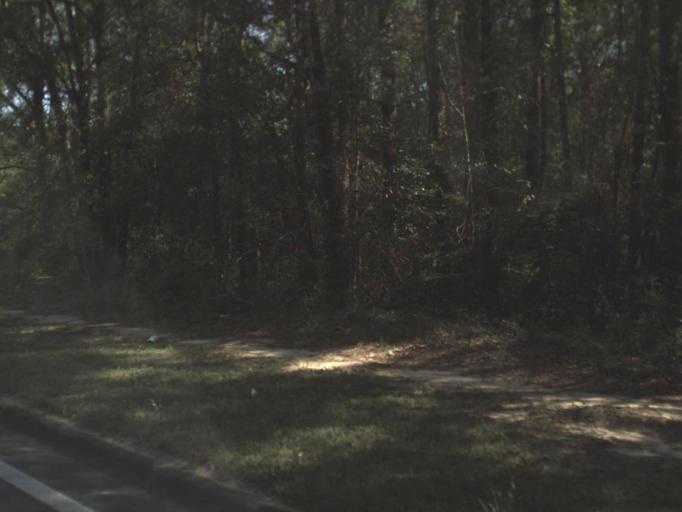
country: US
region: Florida
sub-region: Okaloosa County
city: Crestview
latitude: 30.7611
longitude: -86.5551
